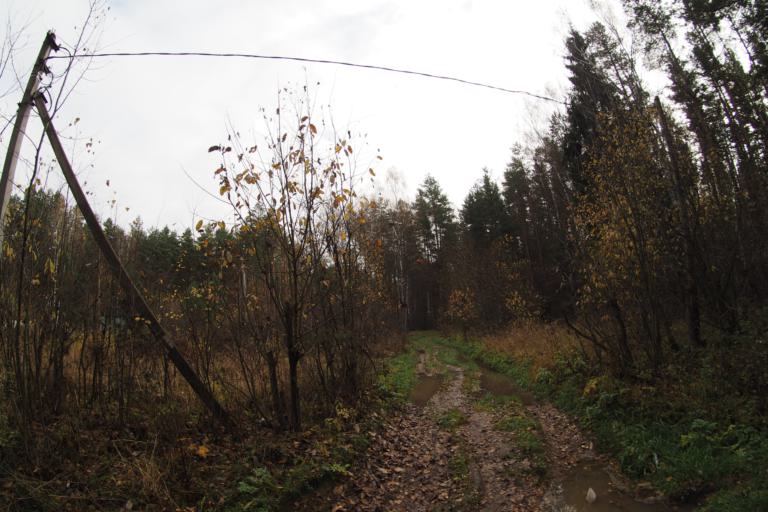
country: RU
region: Moskovskaya
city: Davydovo
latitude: 55.5794
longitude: 38.7541
